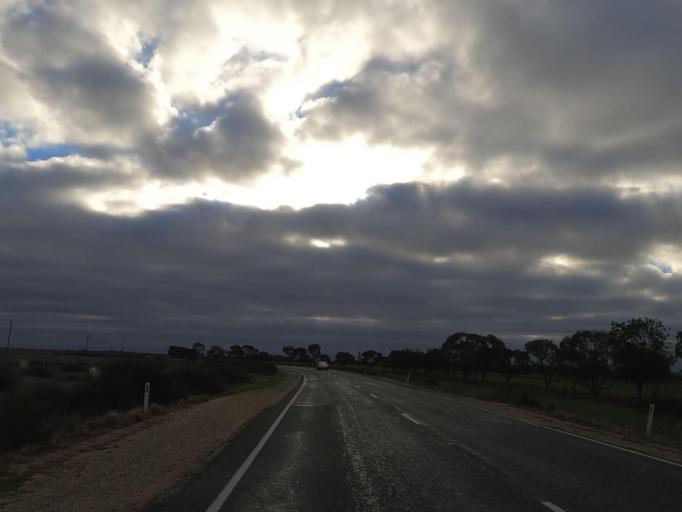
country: AU
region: Victoria
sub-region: Swan Hill
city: Swan Hill
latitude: -35.6518
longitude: 143.8451
